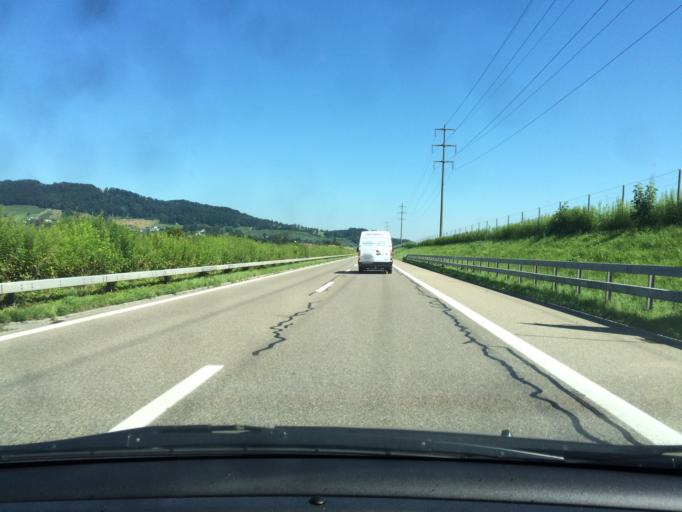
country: AT
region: Vorarlberg
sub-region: Politischer Bezirk Dornbirn
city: Lustenau
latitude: 47.4175
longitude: 9.6472
